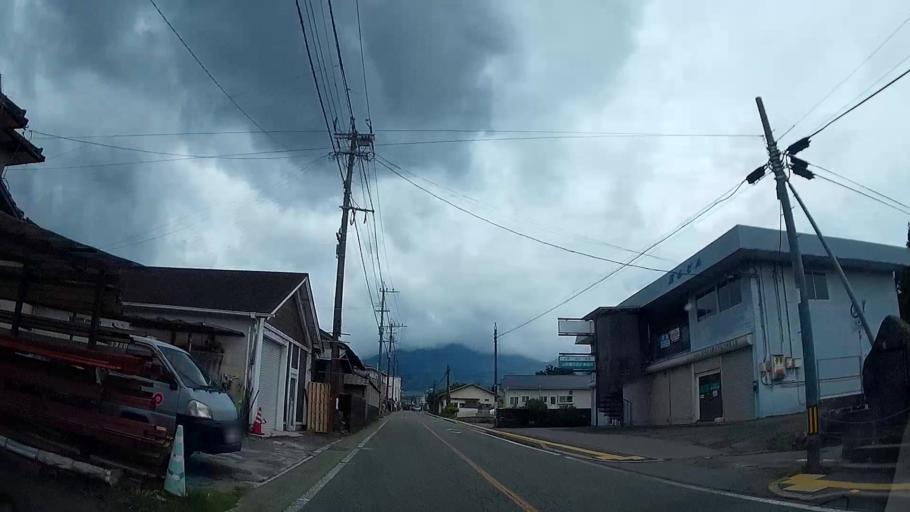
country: JP
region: Kumamoto
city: Aso
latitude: 32.9436
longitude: 131.1177
